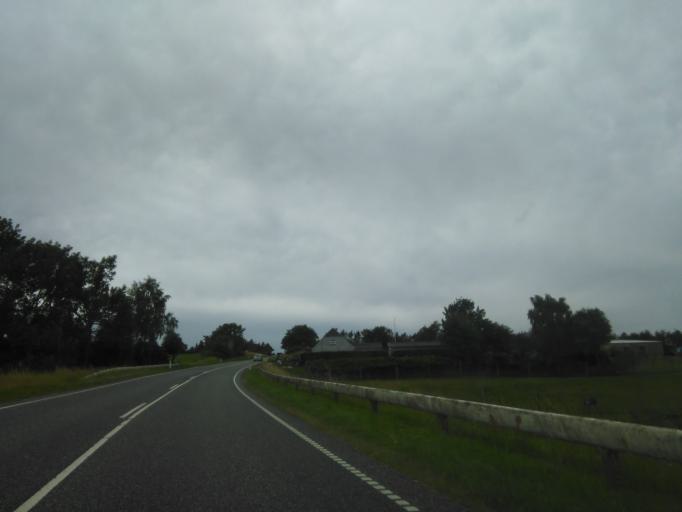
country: DK
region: Central Jutland
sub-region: Skanderborg Kommune
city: Stilling
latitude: 55.9726
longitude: 10.0082
